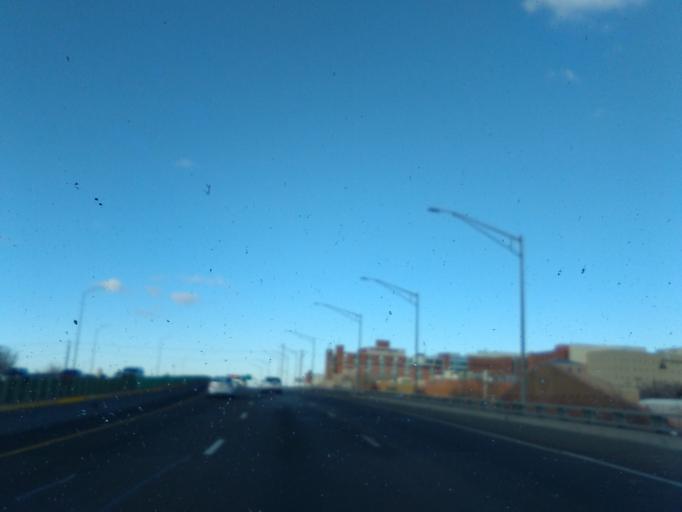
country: US
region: New Mexico
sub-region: Bernalillo County
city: Albuquerque
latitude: 35.0784
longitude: -106.6374
